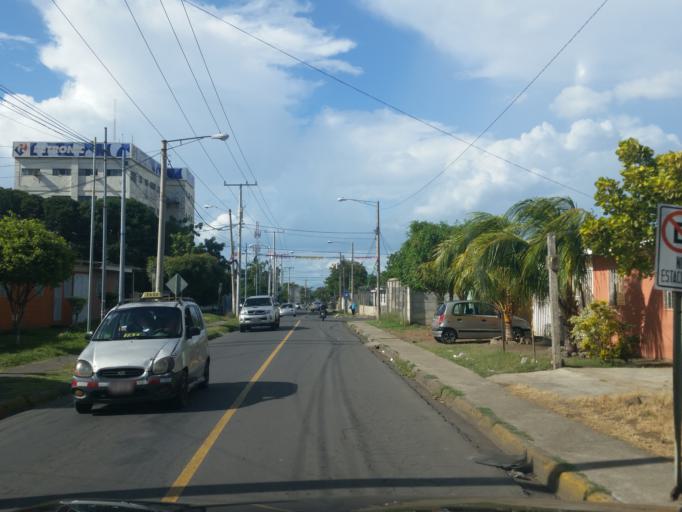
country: NI
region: Managua
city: Managua
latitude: 12.1517
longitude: -86.2680
